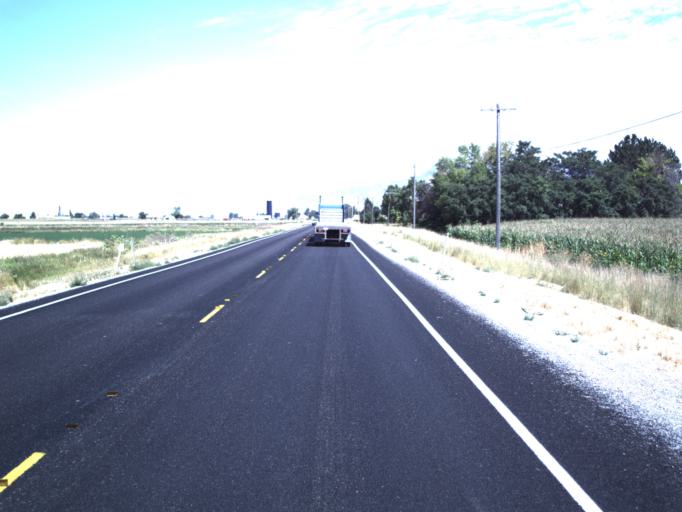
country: US
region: Utah
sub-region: Box Elder County
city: Garland
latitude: 41.7601
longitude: -112.1485
